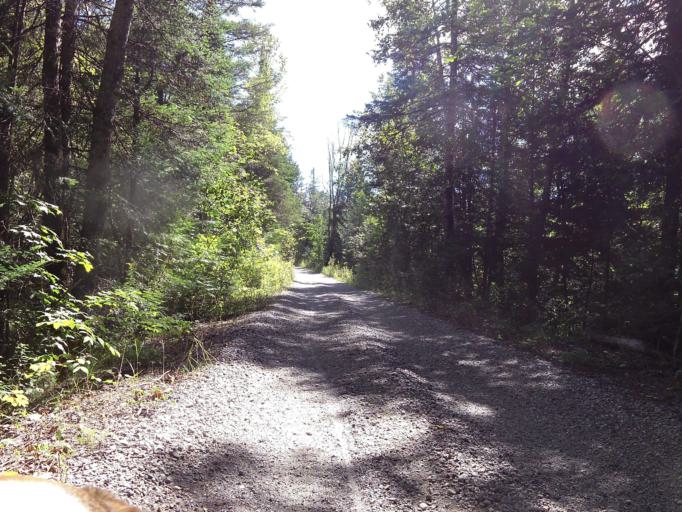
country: CA
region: Ontario
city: Renfrew
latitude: 45.0215
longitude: -76.7041
